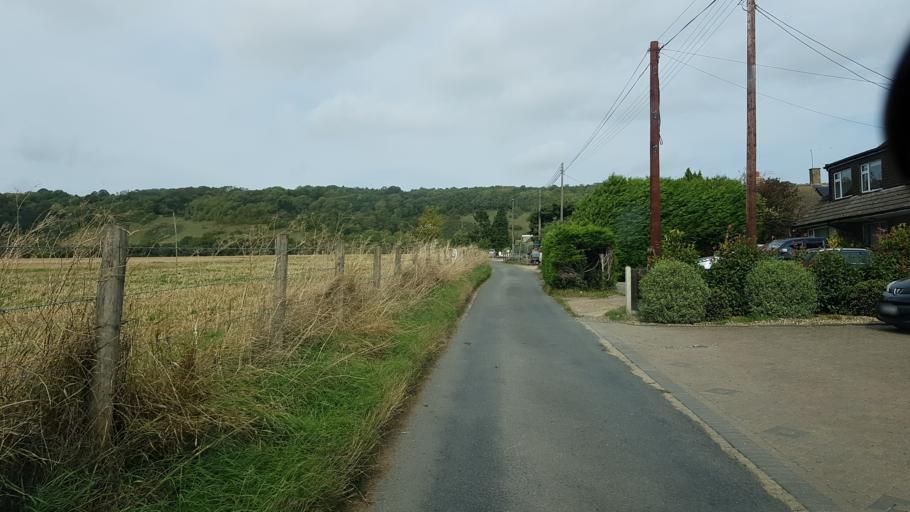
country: GB
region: England
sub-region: Kent
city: Meopham
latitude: 51.3204
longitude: 0.3658
